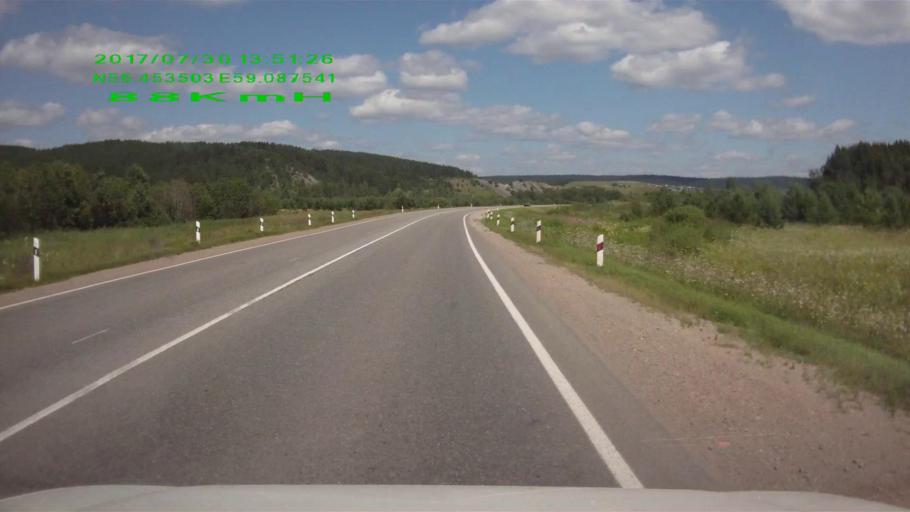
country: RU
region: Sverdlovsk
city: Mikhaylovsk
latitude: 56.4540
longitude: 59.0883
